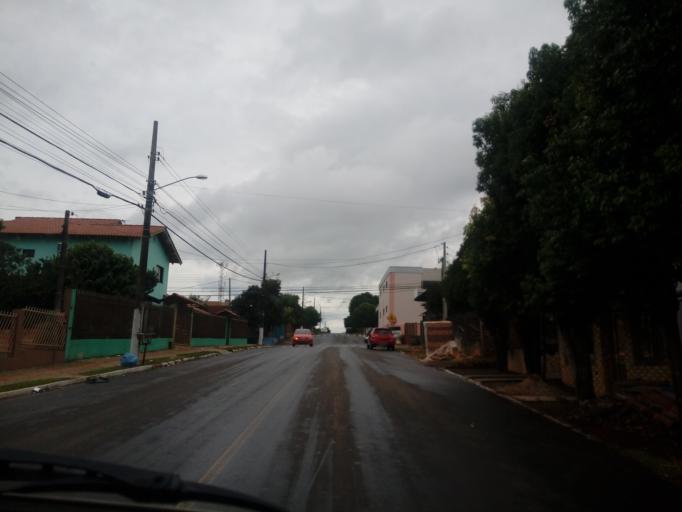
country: BR
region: Santa Catarina
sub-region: Chapeco
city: Chapeco
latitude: -27.0977
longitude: -52.6744
